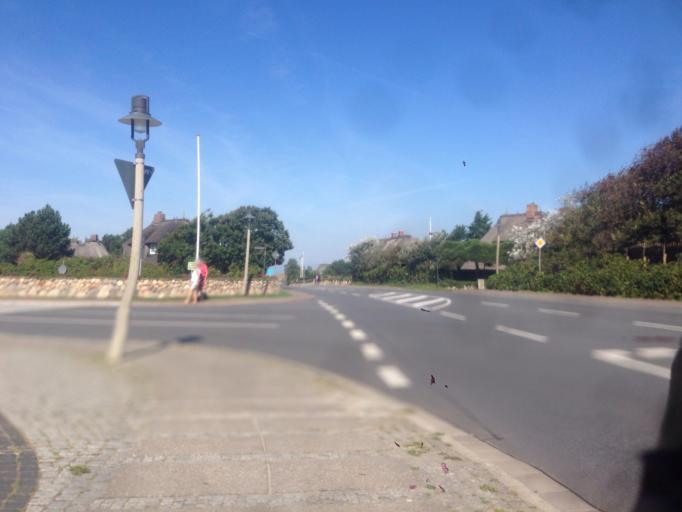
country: DE
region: Schleswig-Holstein
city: Tinnum
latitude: 54.9564
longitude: 8.3422
